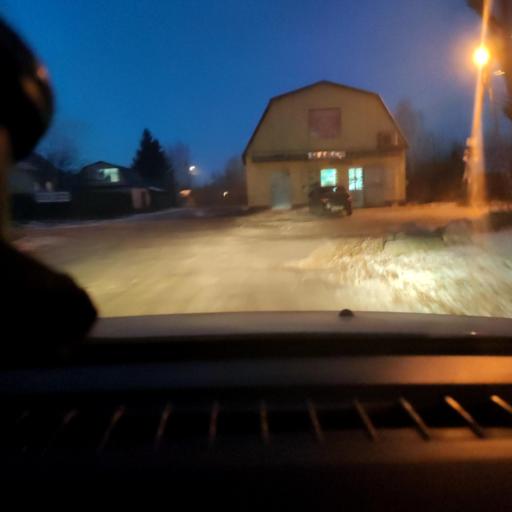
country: RU
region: Samara
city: Petra-Dubrava
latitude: 53.2564
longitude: 50.3390
